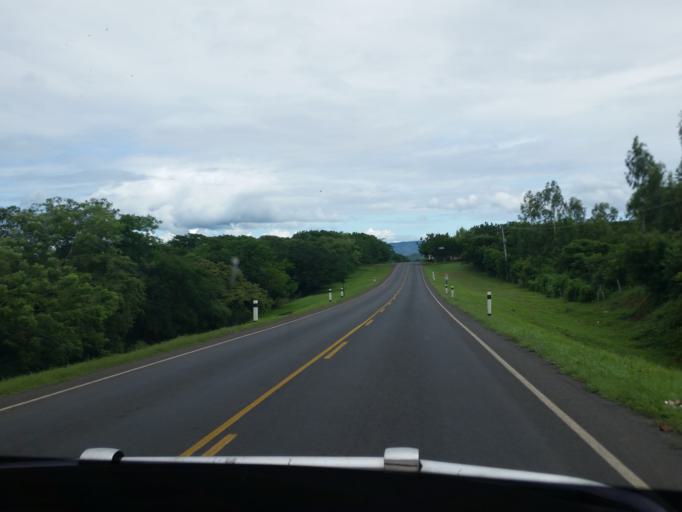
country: NI
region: Managua
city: Tipitapa
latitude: 12.3715
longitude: -86.0468
